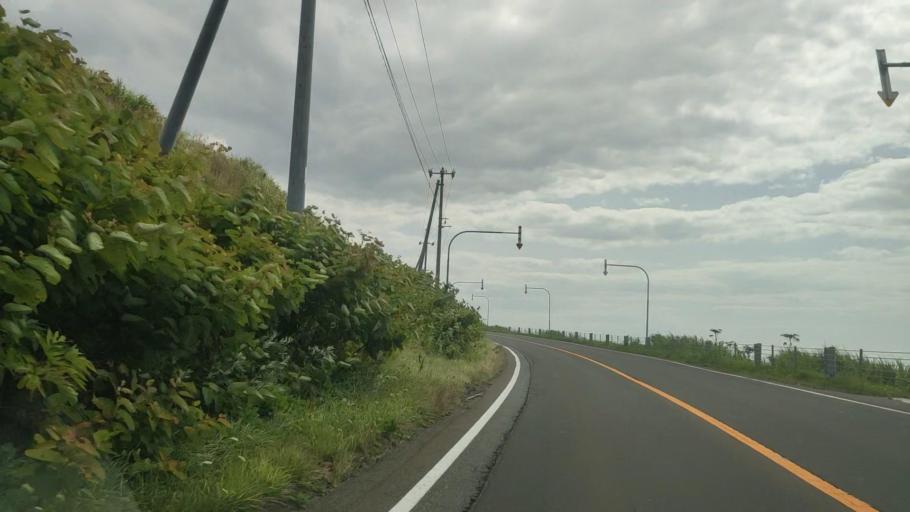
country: JP
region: Hokkaido
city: Rumoi
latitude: 44.5402
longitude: 141.7663
